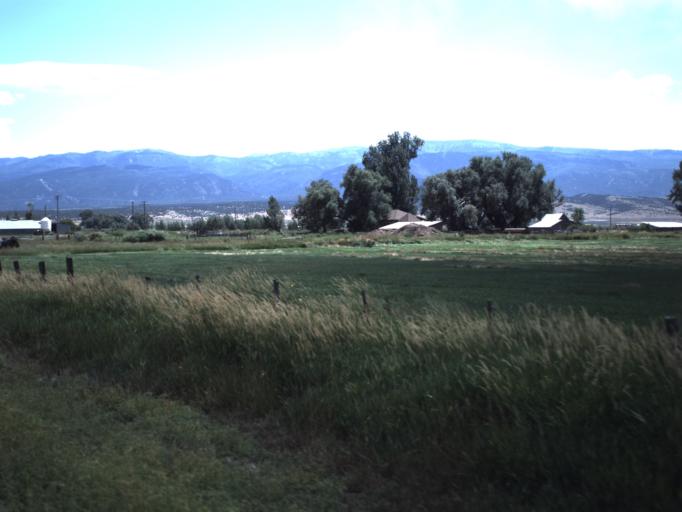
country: US
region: Utah
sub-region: Sanpete County
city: Moroni
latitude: 39.4759
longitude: -111.5749
